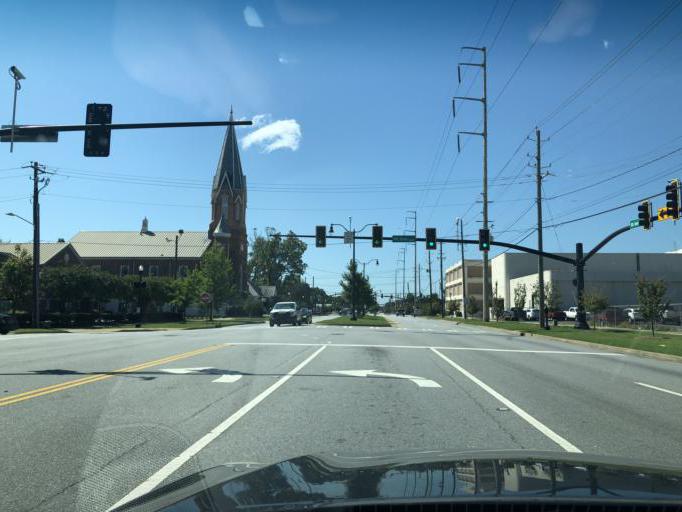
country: US
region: Georgia
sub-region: Muscogee County
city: Columbus
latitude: 32.4663
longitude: -84.9849
